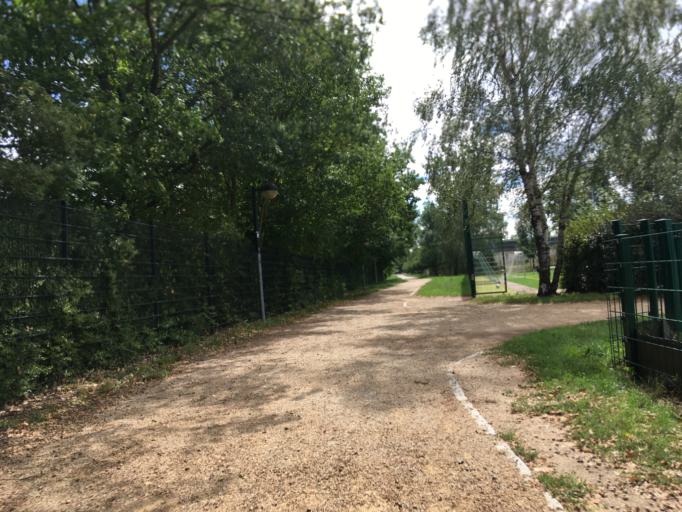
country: DE
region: Berlin
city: Staaken
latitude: 52.5334
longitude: 13.1306
